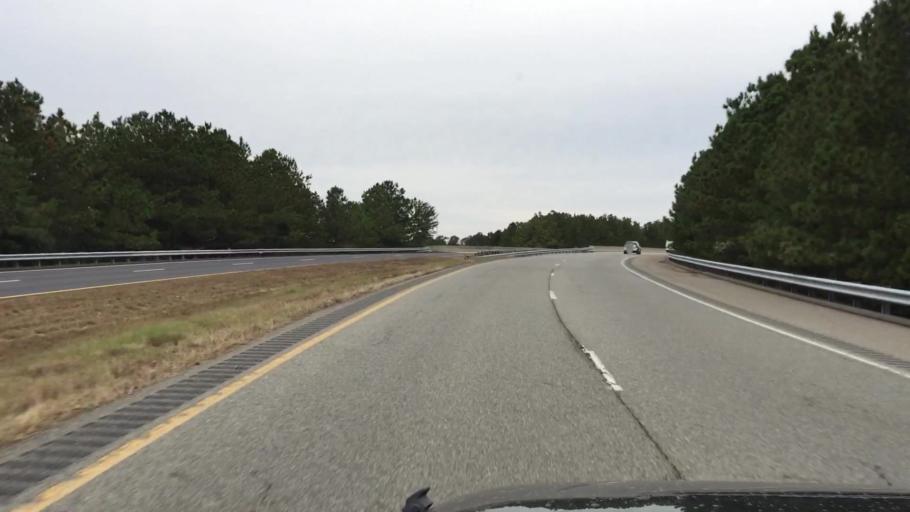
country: US
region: Virginia
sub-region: James City County
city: Williamsburg
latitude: 37.2721
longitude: -76.7513
